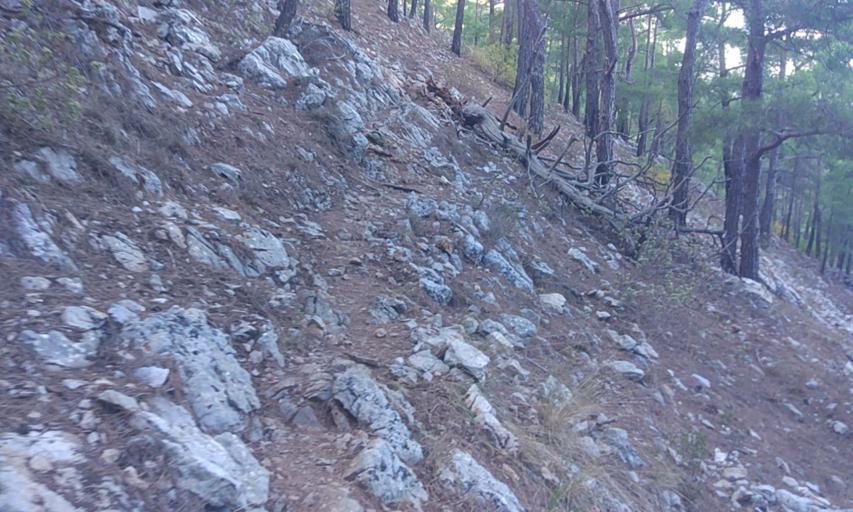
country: TR
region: Antalya
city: Tekirova
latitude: 36.3630
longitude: 30.4787
